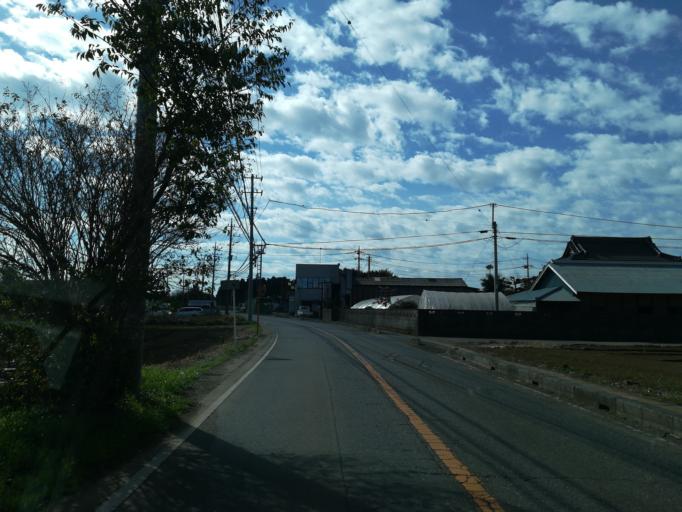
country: JP
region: Ibaraki
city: Naka
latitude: 36.0624
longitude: 140.0874
